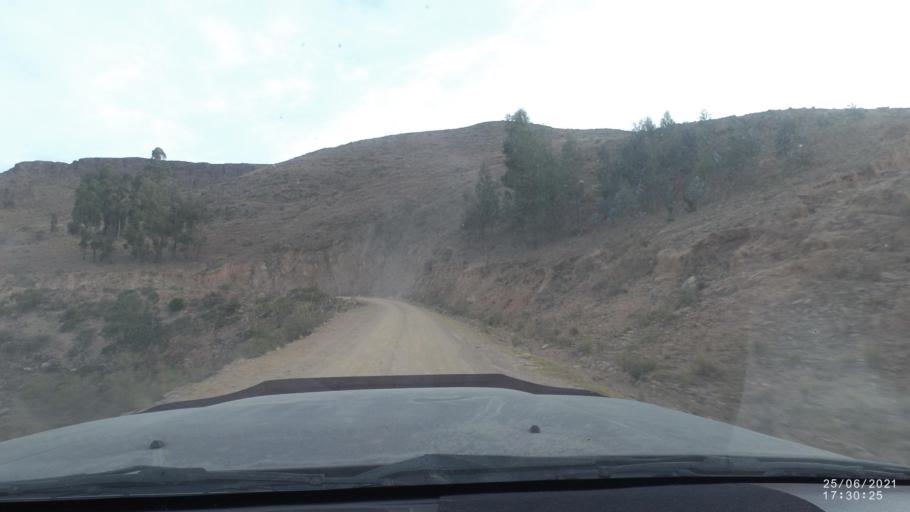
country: BO
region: Cochabamba
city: Mizque
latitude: -17.9336
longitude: -65.6655
